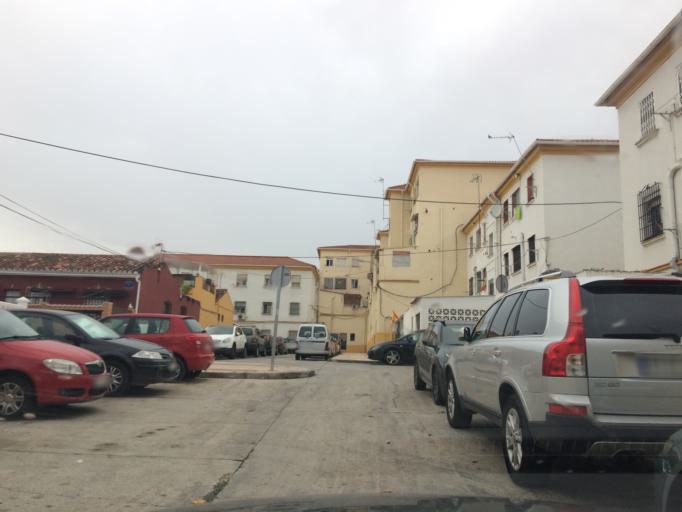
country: ES
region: Andalusia
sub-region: Provincia de Malaga
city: Malaga
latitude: 36.7171
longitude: -4.4423
